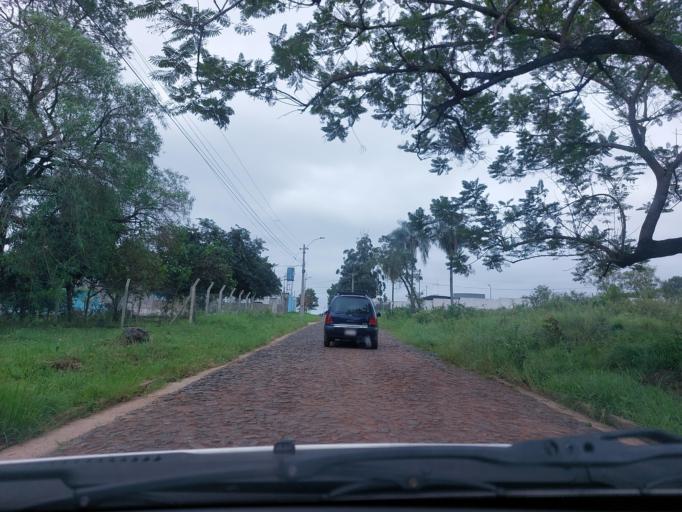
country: PY
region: San Pedro
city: Guayaybi
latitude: -24.6662
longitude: -56.4320
